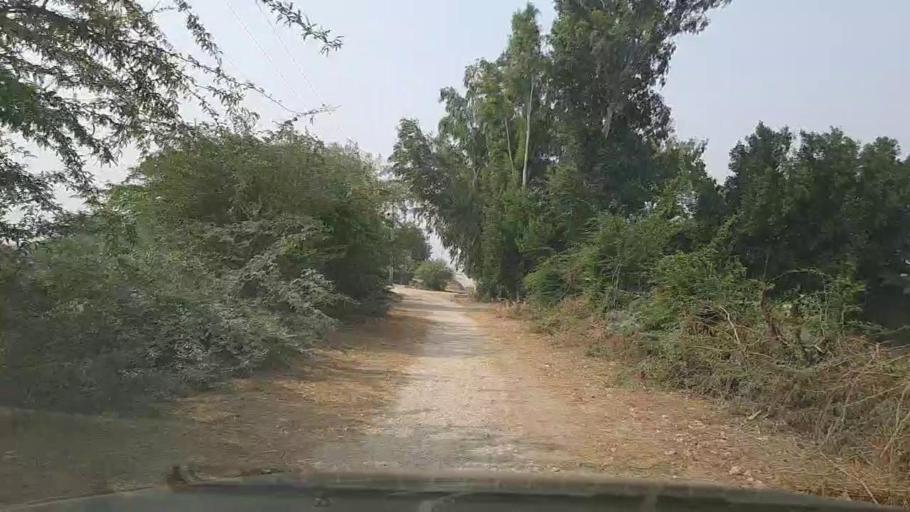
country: PK
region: Sindh
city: Mirpur Sakro
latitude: 24.5468
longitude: 67.8149
